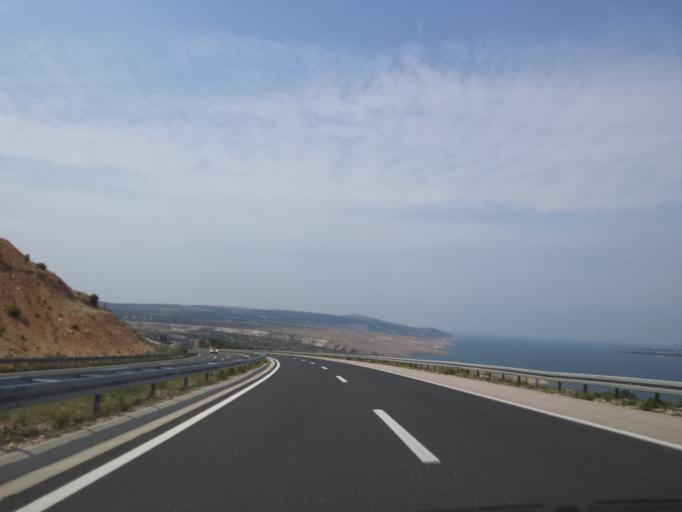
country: HR
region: Zadarska
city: Pridraga
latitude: 44.2422
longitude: 15.5496
